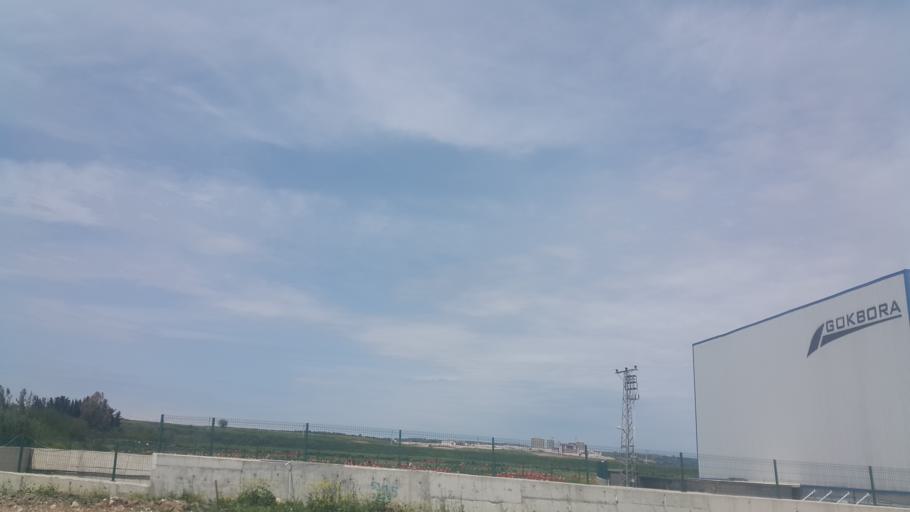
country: TR
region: Adana
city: Yakapinar
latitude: 36.9689
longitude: 35.5444
